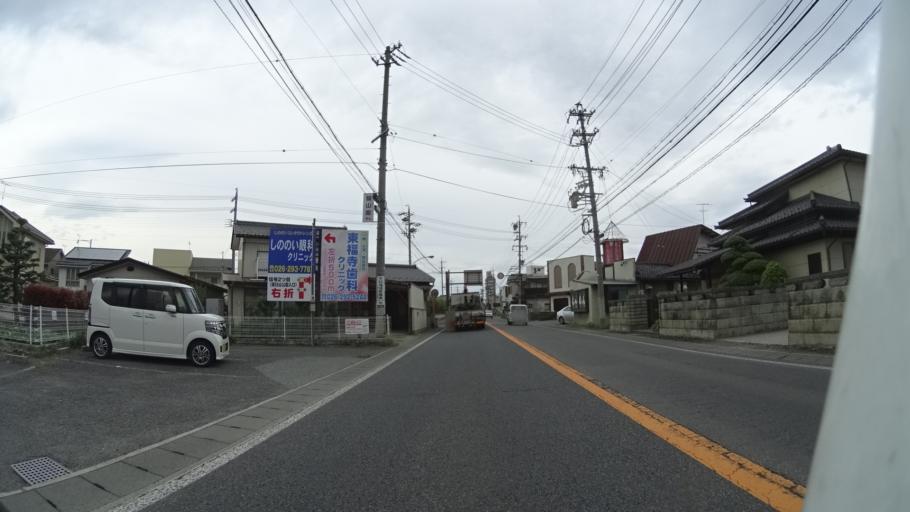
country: JP
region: Nagano
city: Nagano-shi
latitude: 36.5786
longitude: 138.1464
